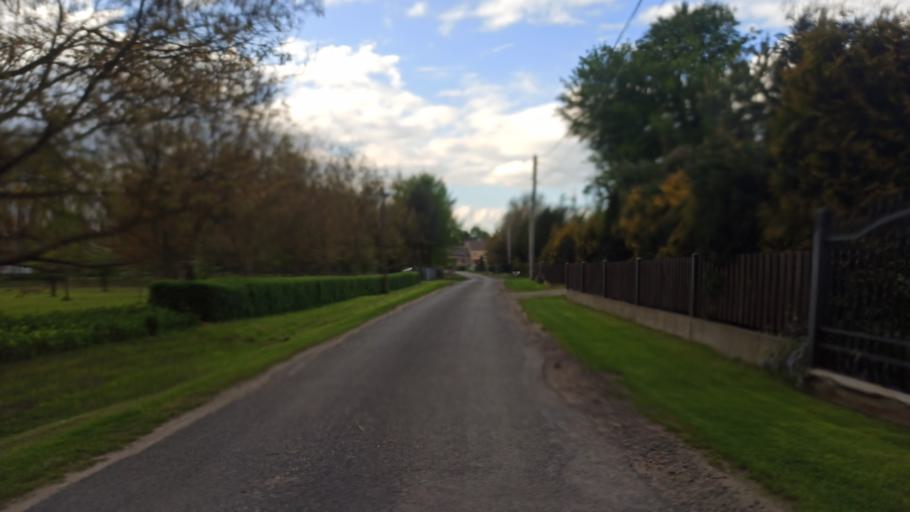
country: PL
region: Subcarpathian Voivodeship
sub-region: Powiat jaroslawski
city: Sosnica
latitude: 49.9213
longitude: 22.8607
